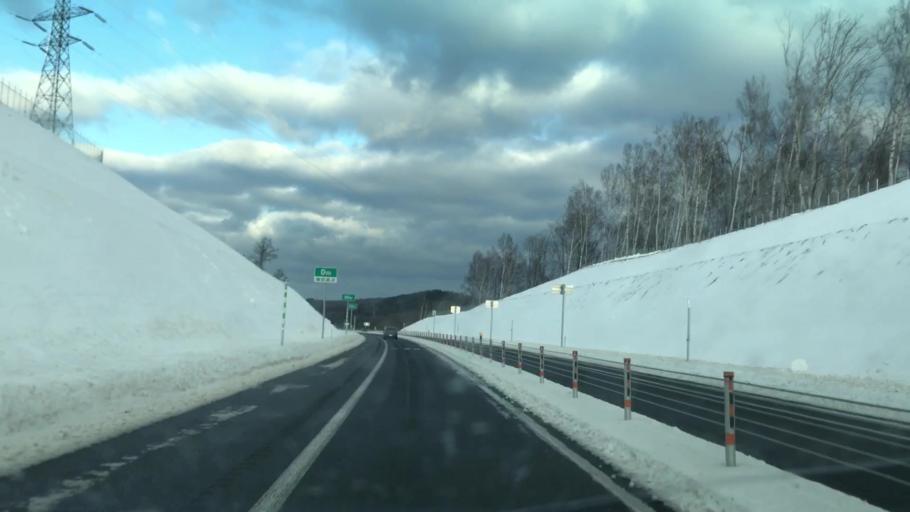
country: JP
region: Hokkaido
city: Otaru
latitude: 43.1916
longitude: 140.9567
